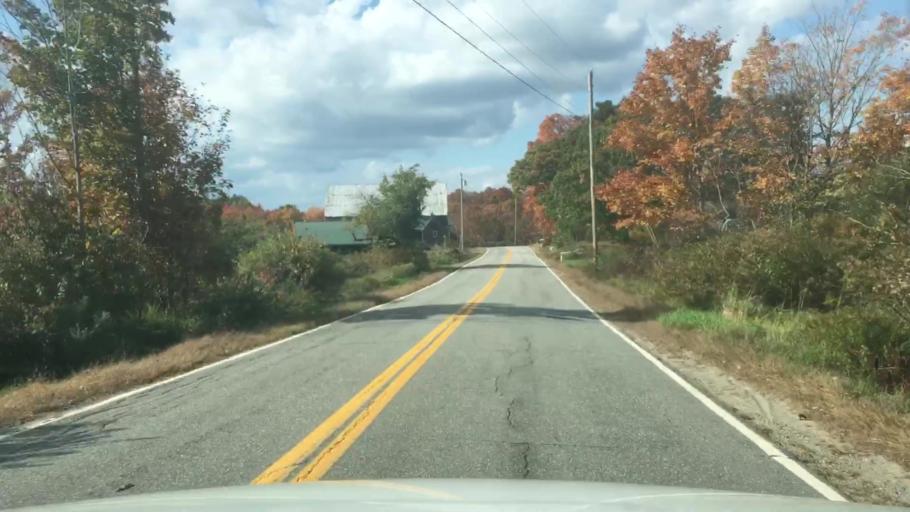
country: US
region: Maine
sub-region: Knox County
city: Washington
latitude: 44.3062
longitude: -69.3376
